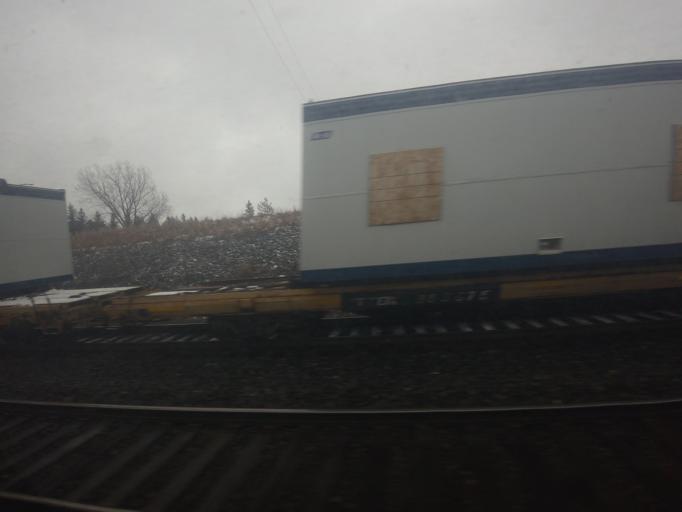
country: CA
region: Ontario
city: Belleville
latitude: 44.1906
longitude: -77.3308
